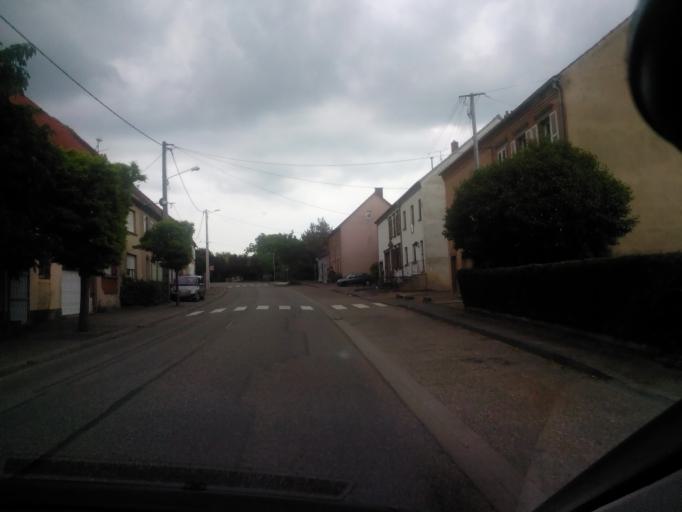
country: FR
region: Alsace
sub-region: Departement du Bas-Rhin
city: Keskastel
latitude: 48.9666
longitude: 7.0434
